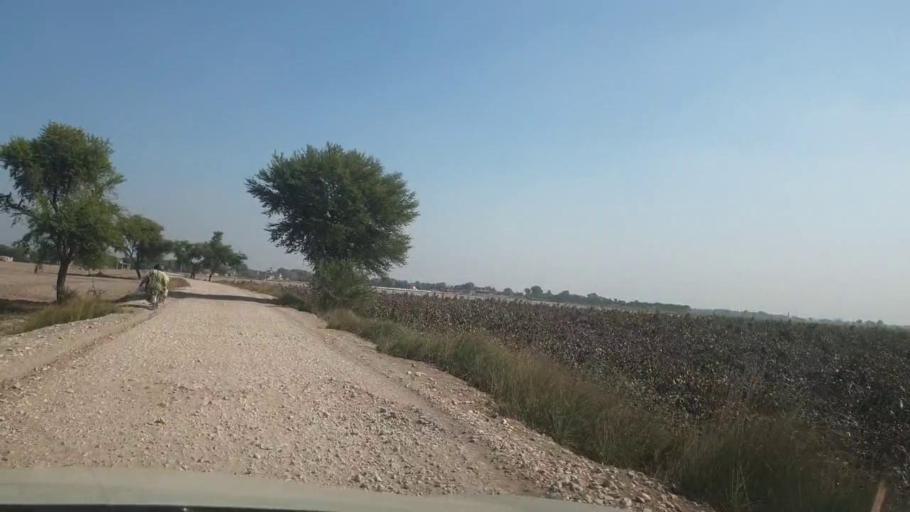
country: PK
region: Sindh
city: Bhan
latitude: 26.5767
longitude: 67.6807
